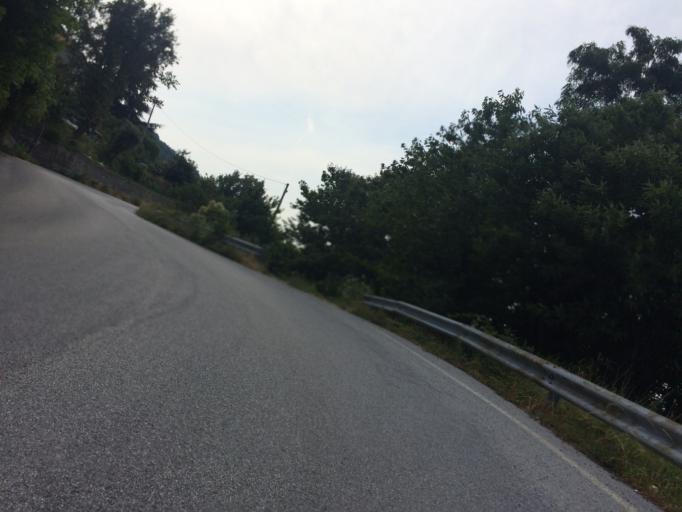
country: IT
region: Liguria
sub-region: Provincia di Savona
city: San Giovanni
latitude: 44.3995
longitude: 8.4938
